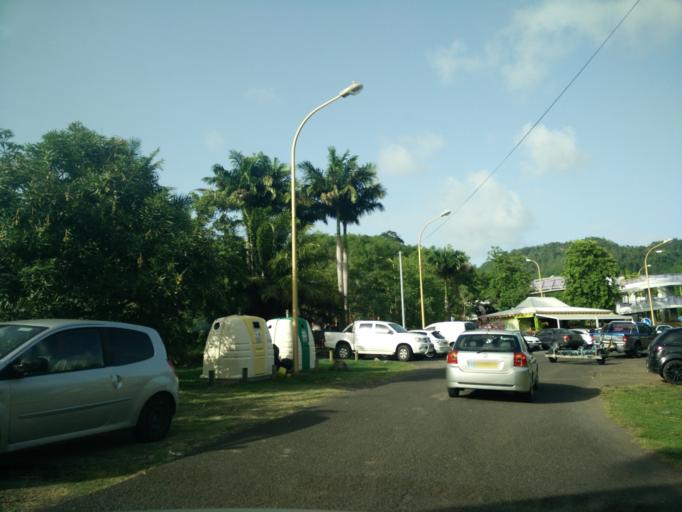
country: MQ
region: Martinique
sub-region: Martinique
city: Riviere-Pilote
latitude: 14.4696
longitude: -60.9079
